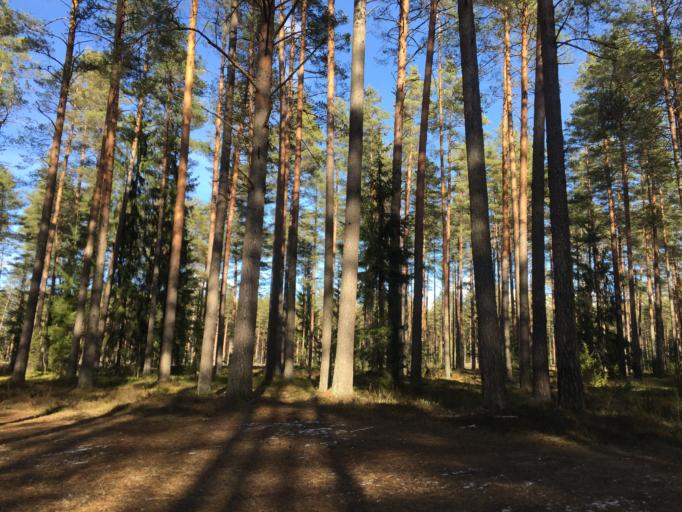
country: LV
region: Garkalne
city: Garkalne
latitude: 56.9582
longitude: 24.4435
